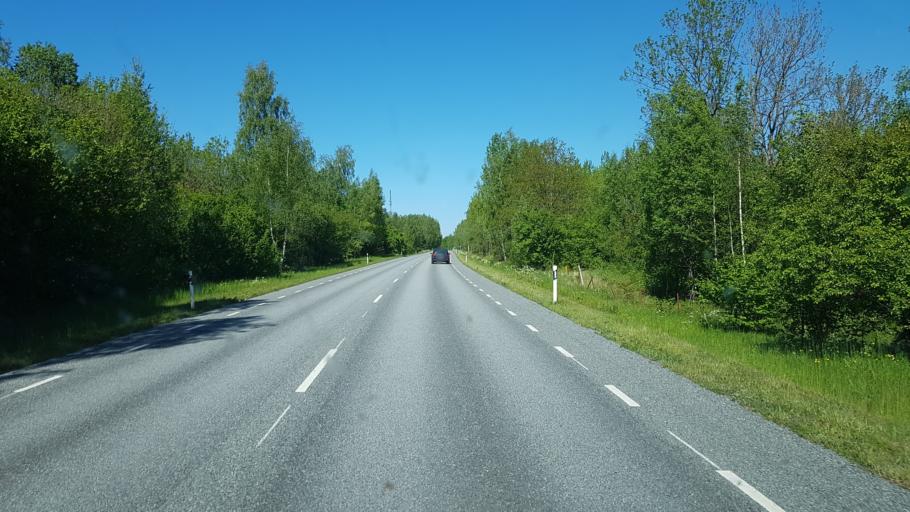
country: EE
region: Saare
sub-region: Orissaare vald
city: Orissaare
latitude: 58.5406
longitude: 23.0514
